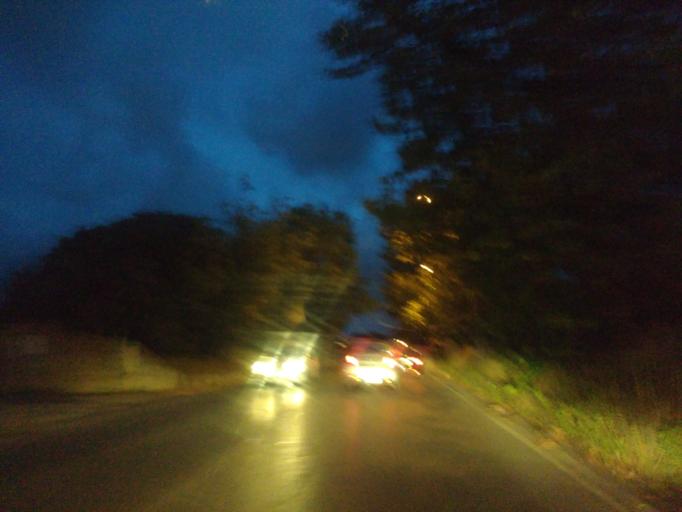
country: IT
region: Latium
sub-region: Citta metropolitana di Roma Capitale
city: Anzio
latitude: 41.4591
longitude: 12.6212
